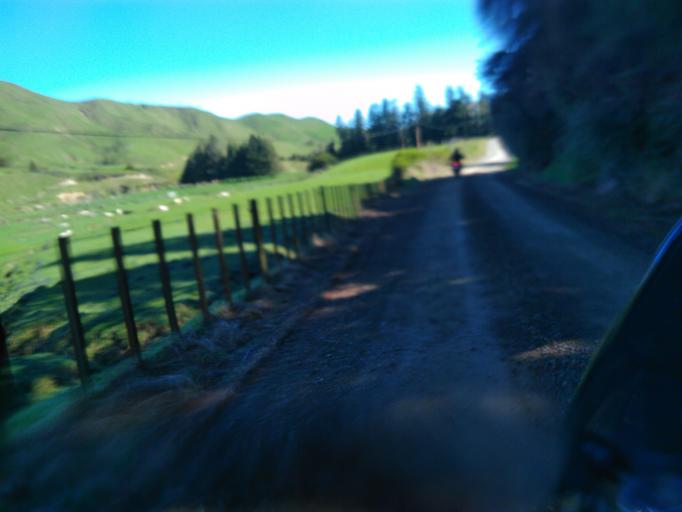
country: NZ
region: Bay of Plenty
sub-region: Opotiki District
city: Opotiki
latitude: -38.2926
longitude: 177.5482
